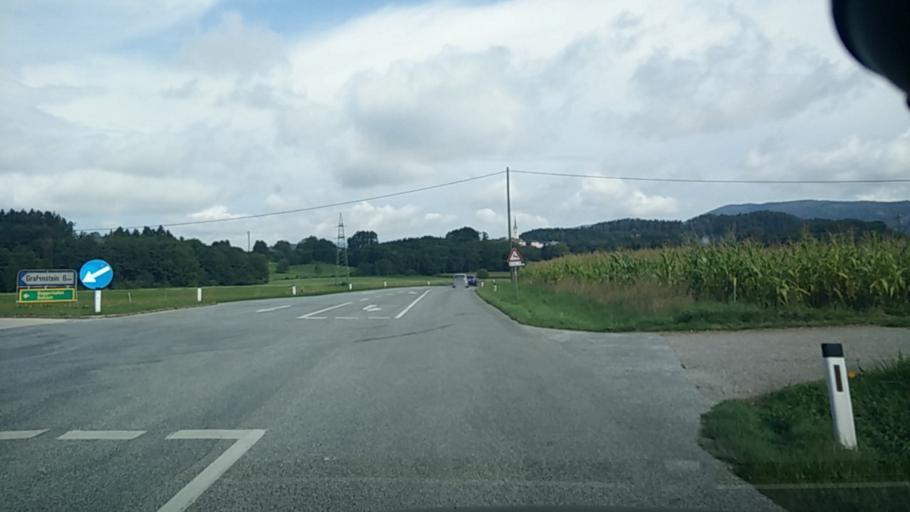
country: AT
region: Carinthia
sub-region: Politischer Bezirk Volkermarkt
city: Gallizien
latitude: 46.6237
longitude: 14.5461
